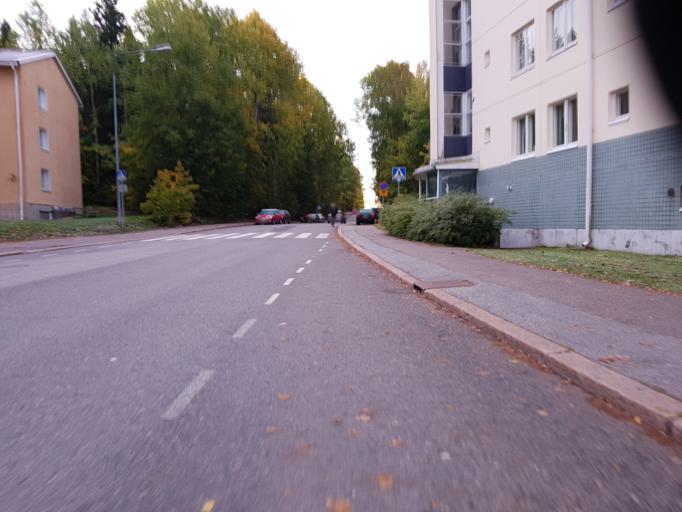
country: FI
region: Uusimaa
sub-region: Helsinki
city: Helsinki
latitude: 60.2253
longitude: 24.9305
